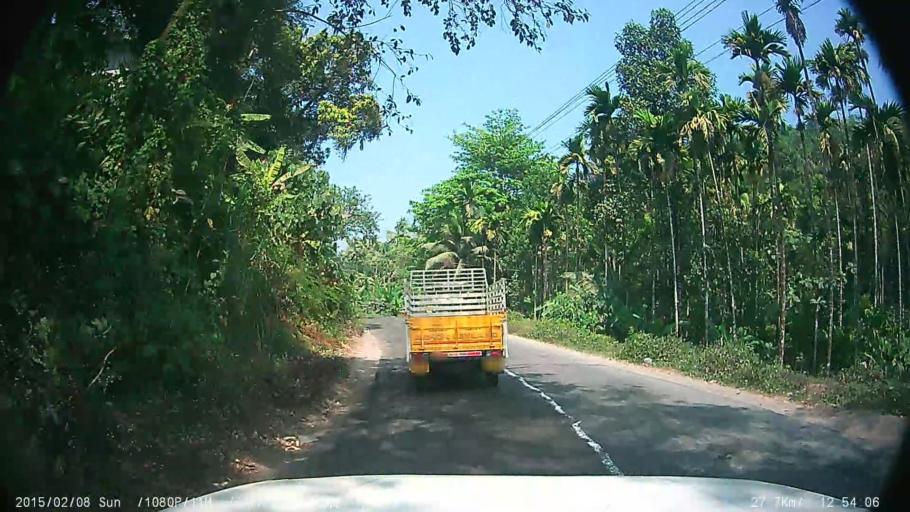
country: IN
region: Kerala
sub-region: Ernakulam
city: Piravam
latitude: 9.8730
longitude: 76.5966
